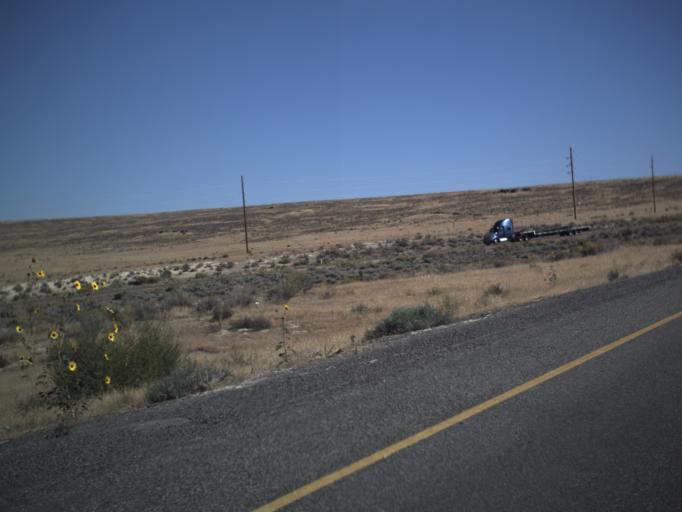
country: US
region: Utah
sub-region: Tooele County
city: Grantsville
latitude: 40.7575
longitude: -113.0164
